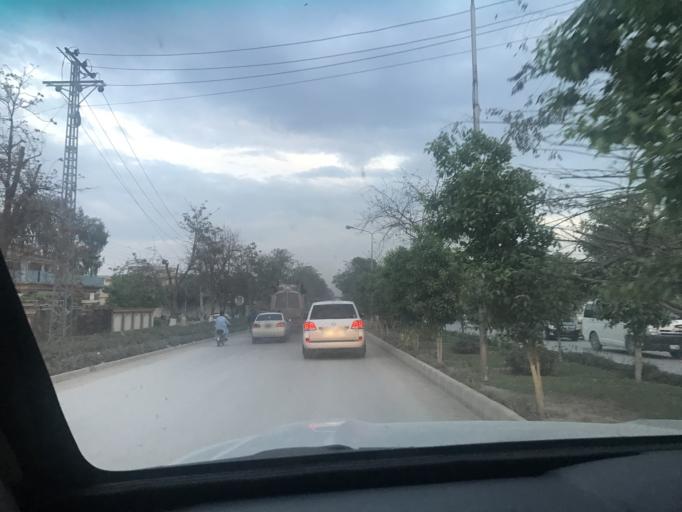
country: PK
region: Khyber Pakhtunkhwa
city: Peshawar
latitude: 33.9778
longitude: 71.4471
